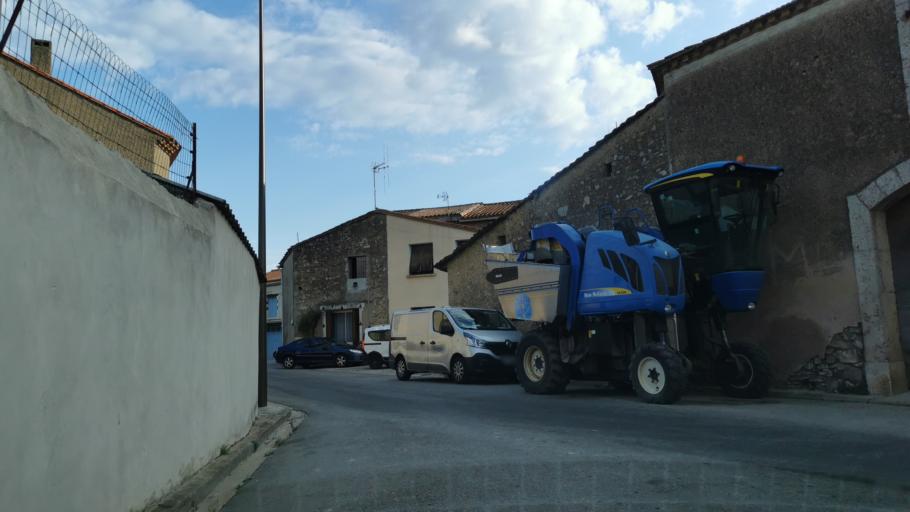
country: FR
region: Languedoc-Roussillon
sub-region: Departement de l'Aude
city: Nevian
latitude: 43.2137
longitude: 2.9027
